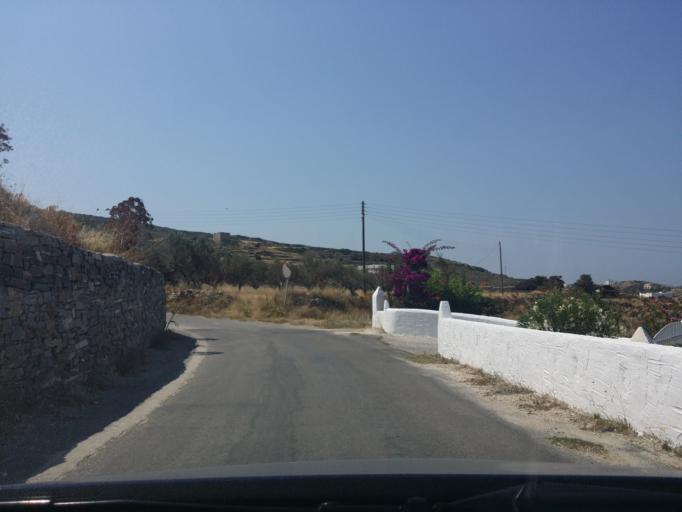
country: GR
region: South Aegean
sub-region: Nomos Kykladon
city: Antiparos
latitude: 37.0462
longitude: 25.1255
